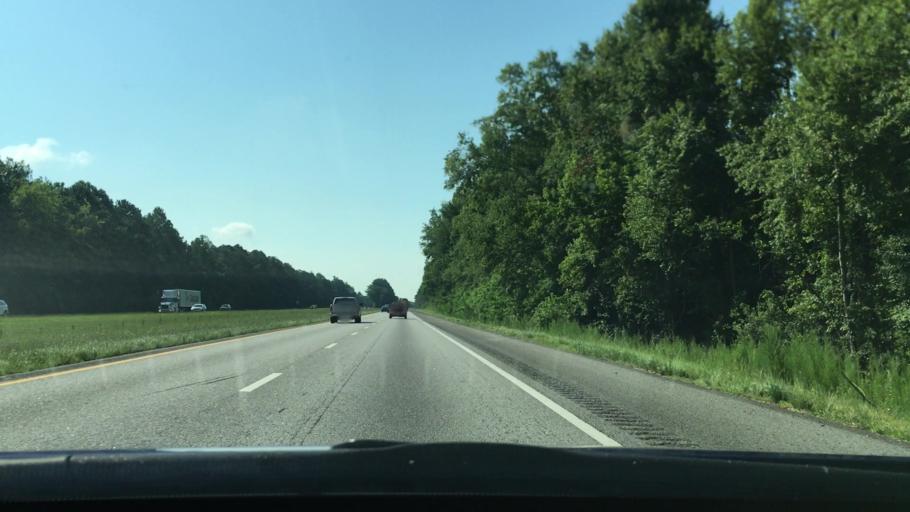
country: US
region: South Carolina
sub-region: Dorchester County
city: Ridgeville
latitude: 33.1794
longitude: -80.3764
